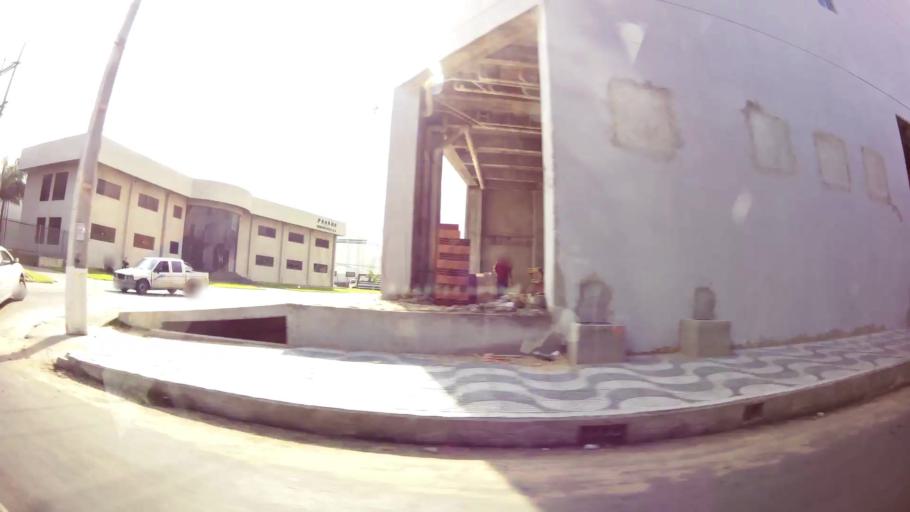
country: PY
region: Central
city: Fernando de la Mora
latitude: -25.3354
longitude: -57.5365
